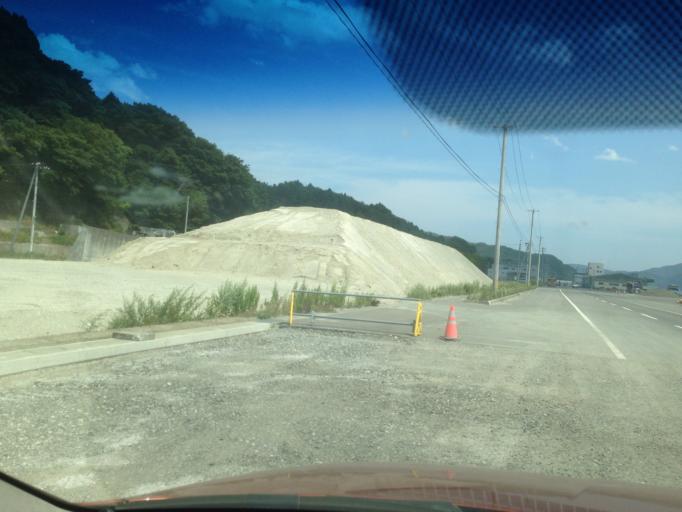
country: JP
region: Iwate
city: Otsuchi
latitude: 39.3558
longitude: 141.9195
